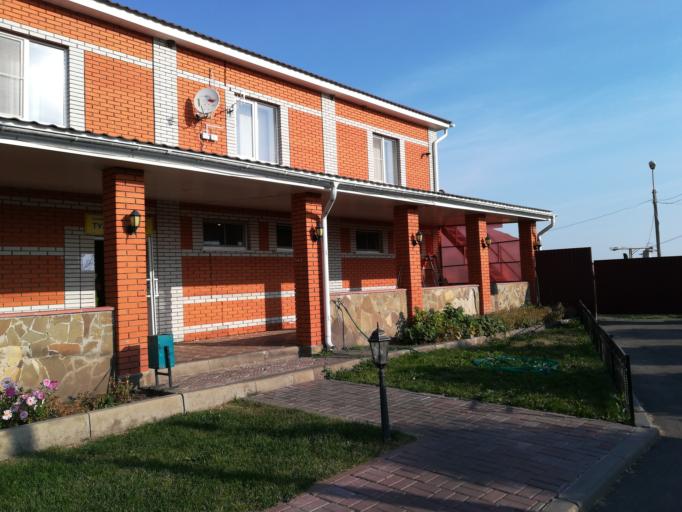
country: RU
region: Tula
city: Volovo
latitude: 53.5015
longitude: 38.1147
